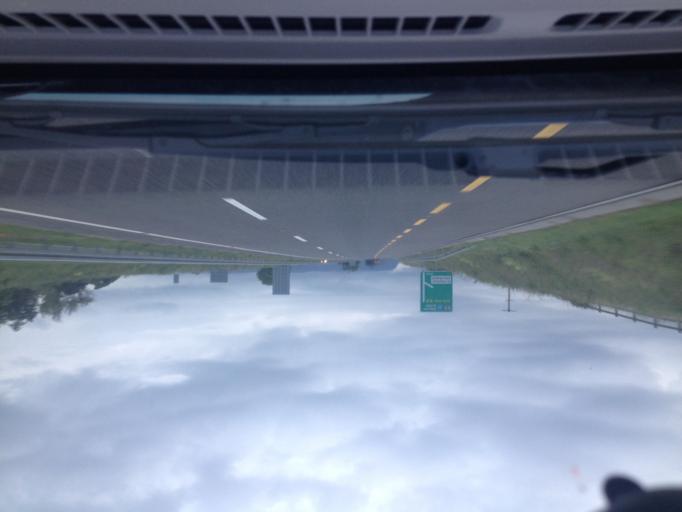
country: IE
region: Connaught
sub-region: Sligo
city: Sligo
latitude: 54.2503
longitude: -8.4773
